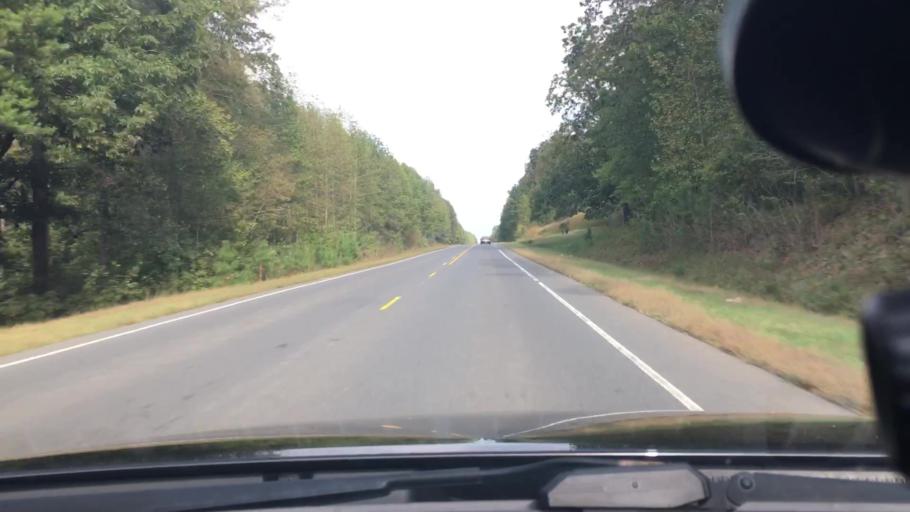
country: US
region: North Carolina
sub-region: Montgomery County
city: Mount Gilead
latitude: 35.3076
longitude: -80.0107
